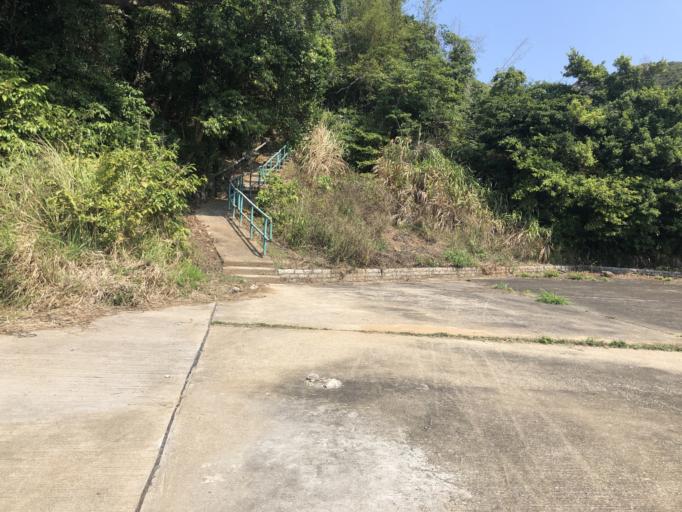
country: HK
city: Sok Kwu Wan
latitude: 22.1654
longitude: 114.2550
